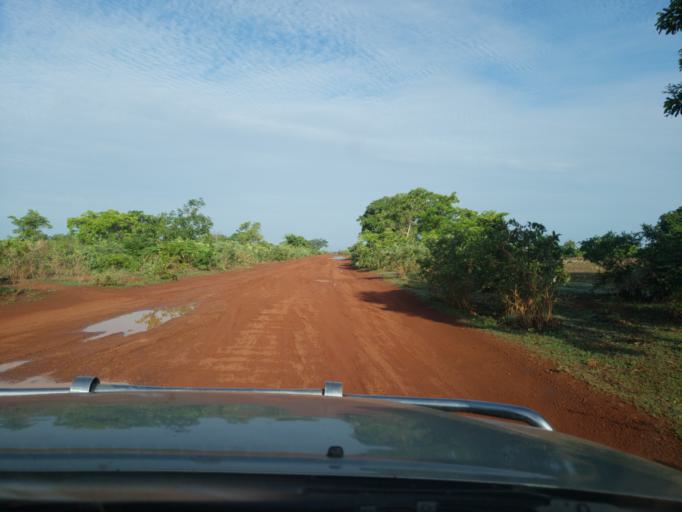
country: ML
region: Sikasso
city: Koutiala
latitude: 12.4268
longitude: -5.6384
